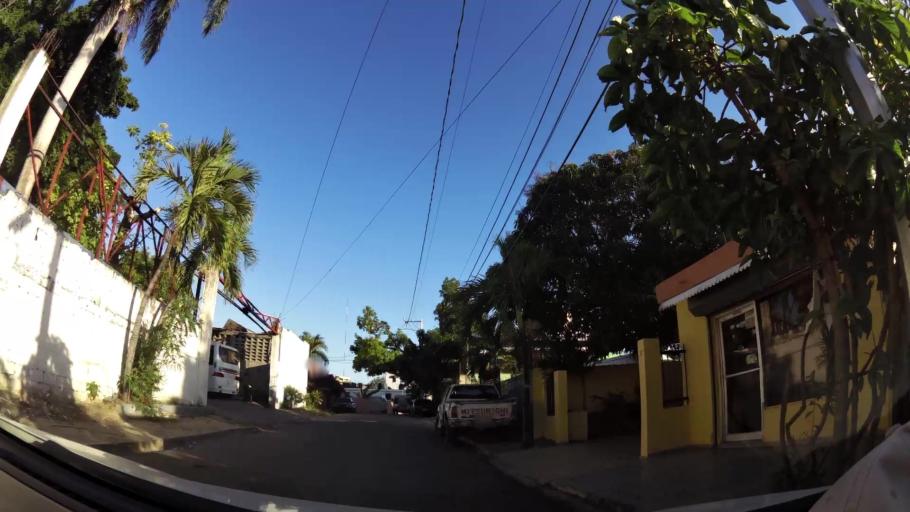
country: DO
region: Nacional
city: Santo Domingo
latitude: 18.4872
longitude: -69.9702
